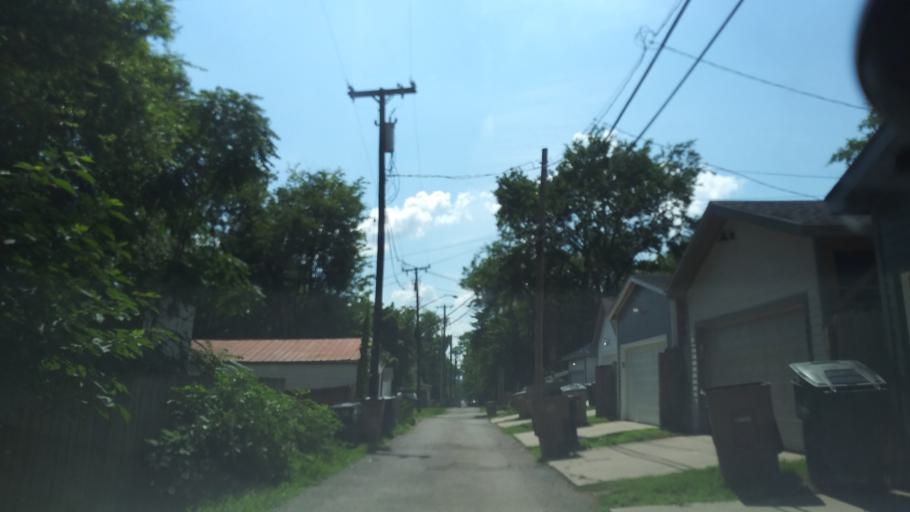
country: US
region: Tennessee
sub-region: Davidson County
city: Nashville
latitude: 36.1583
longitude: -86.8431
